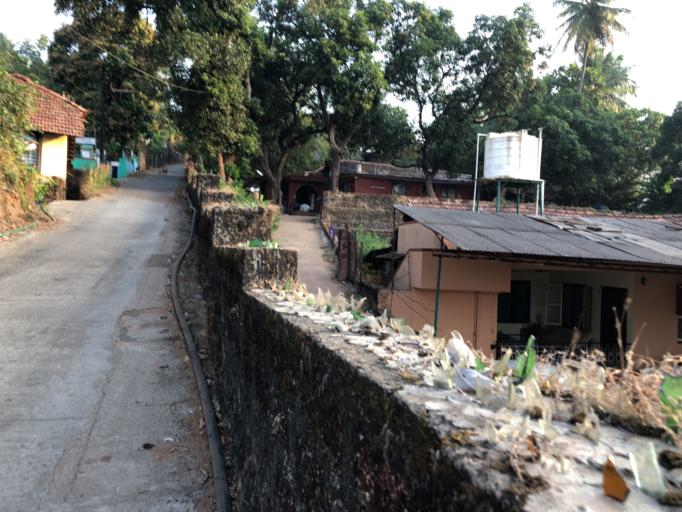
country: IN
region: Karnataka
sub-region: Dakshina Kannada
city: Mangalore
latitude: 12.8701
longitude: 74.8665
